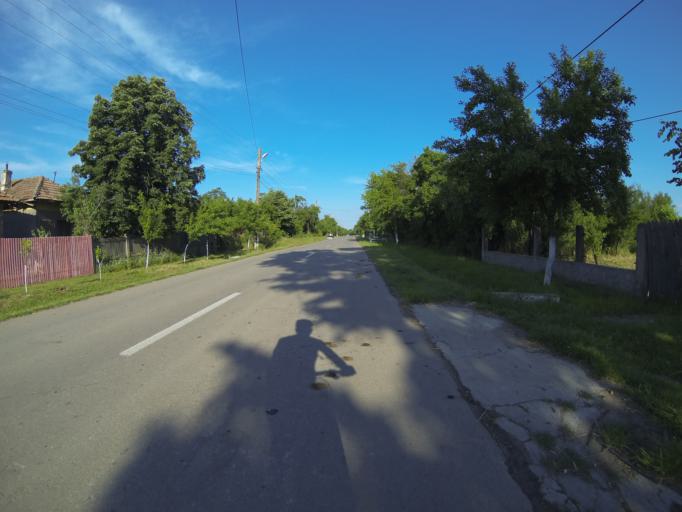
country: RO
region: Dolj
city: Satu Nou Calopar
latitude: 44.1610
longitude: 23.7745
